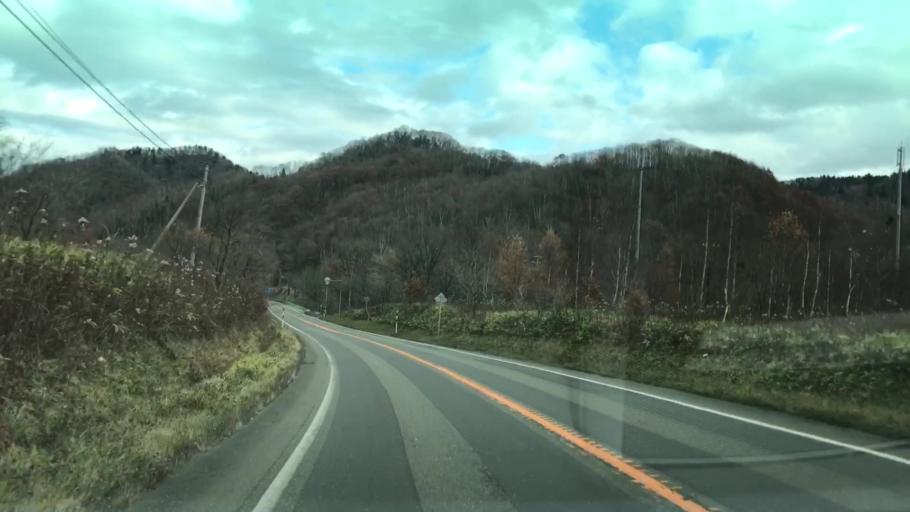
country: JP
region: Hokkaido
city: Shizunai-furukawacho
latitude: 42.8130
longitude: 142.4183
